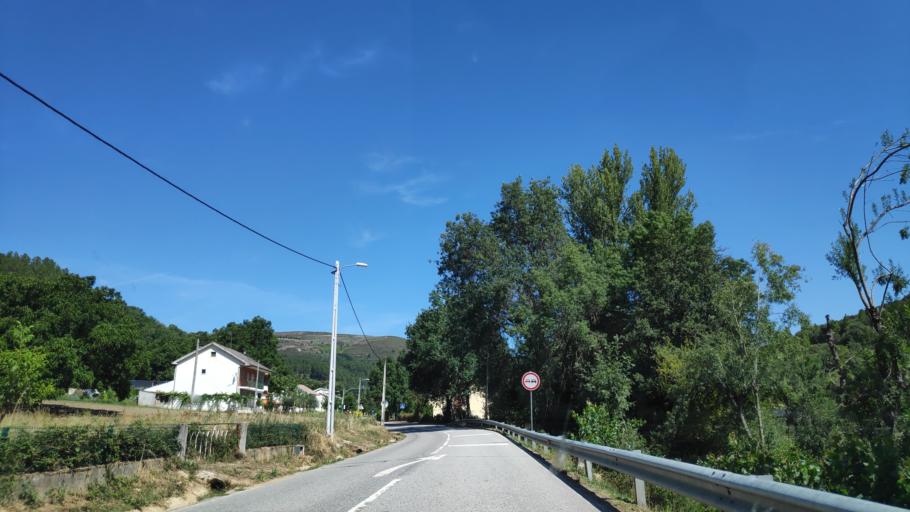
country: PT
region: Braganca
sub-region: Braganca Municipality
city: Braganca
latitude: 41.8641
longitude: -6.7478
